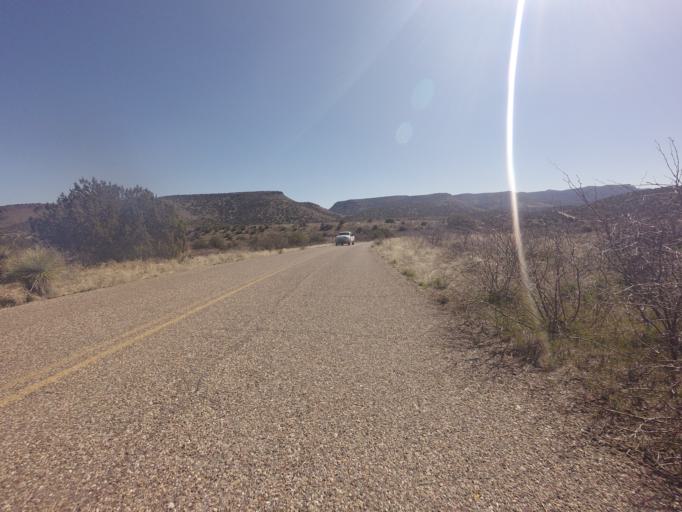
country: US
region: Arizona
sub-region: Yavapai County
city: Lake Montezuma
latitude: 34.6832
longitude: -111.7258
